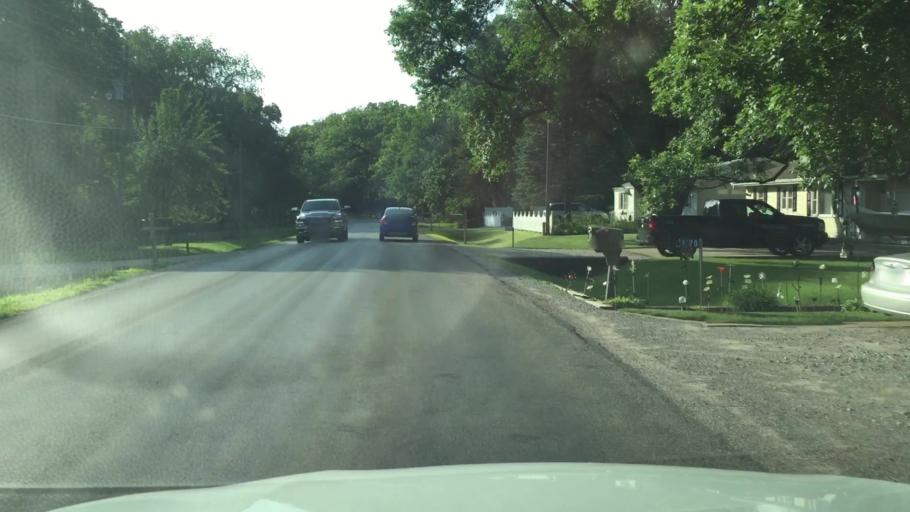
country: US
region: Iowa
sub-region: Linn County
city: Ely
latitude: 41.8287
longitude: -91.6259
